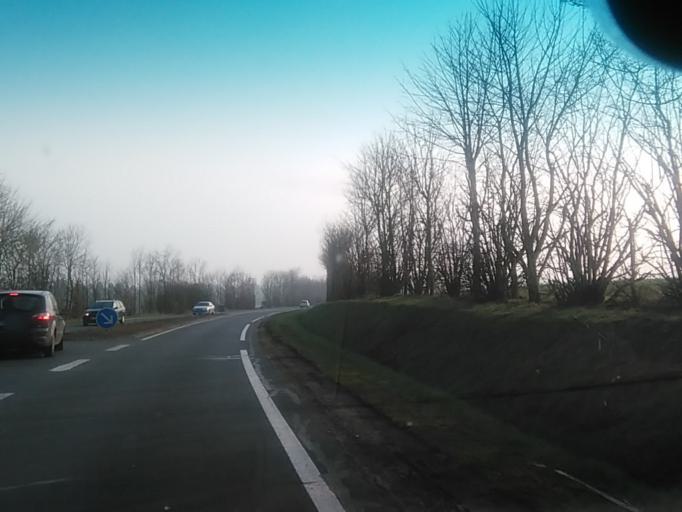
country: FR
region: Lower Normandy
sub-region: Departement du Calvados
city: Bretteville-sur-Odon
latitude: 49.1582
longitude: -0.4117
